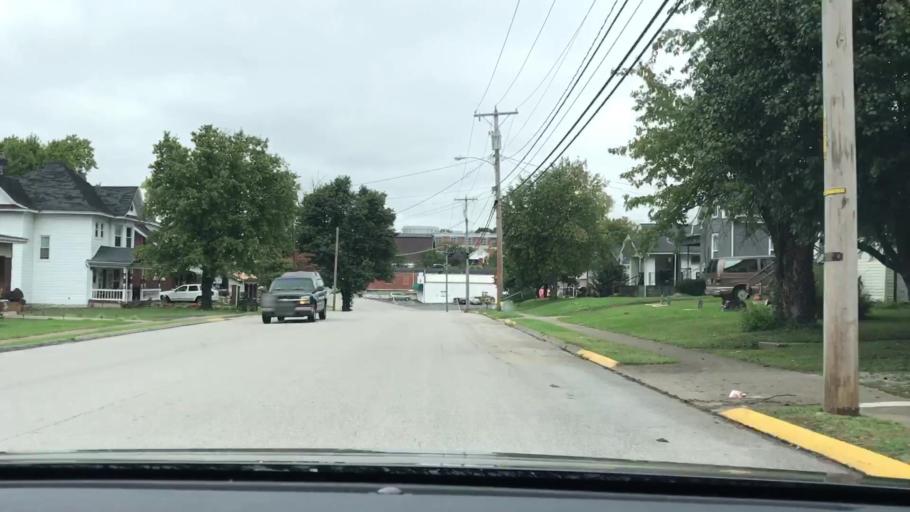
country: US
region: Kentucky
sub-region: Pulaski County
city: Somerset
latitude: 37.0899
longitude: -84.6003
